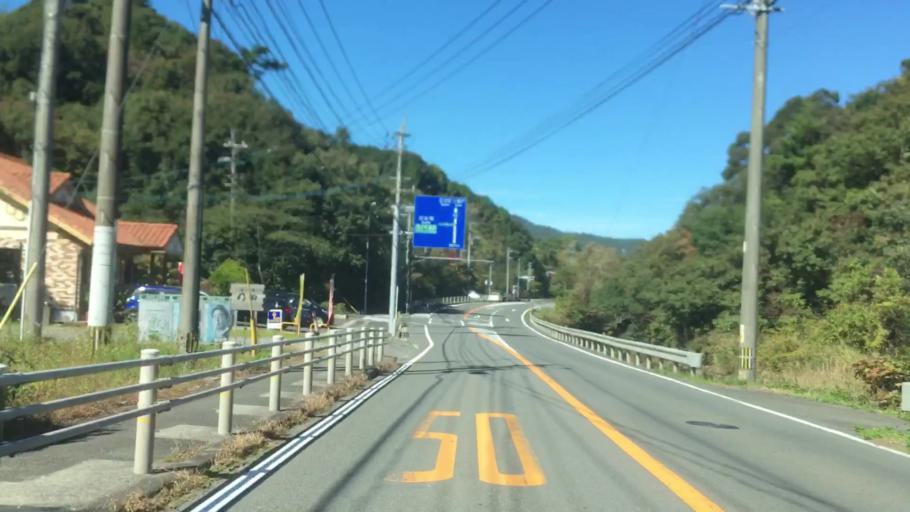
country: JP
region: Nagasaki
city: Sasebo
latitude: 32.9947
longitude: 129.7331
